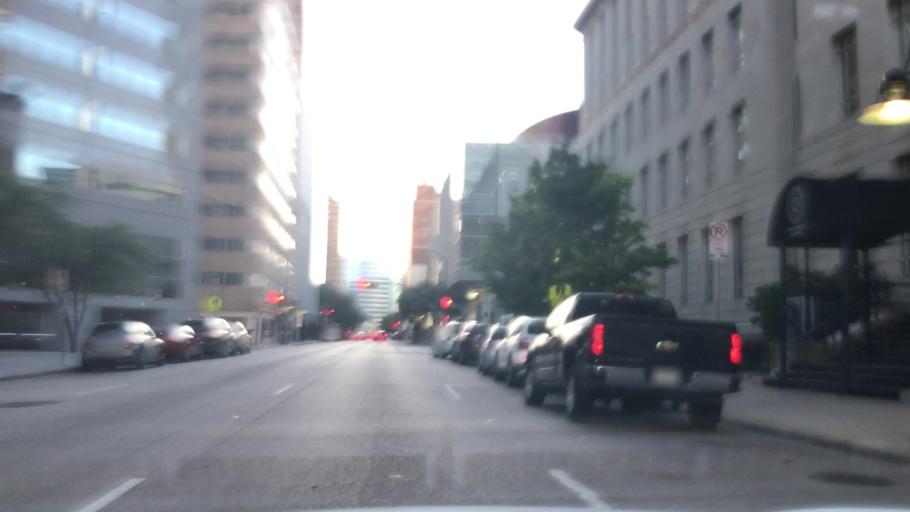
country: US
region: Texas
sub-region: Dallas County
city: Dallas
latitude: 32.7832
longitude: -96.7984
